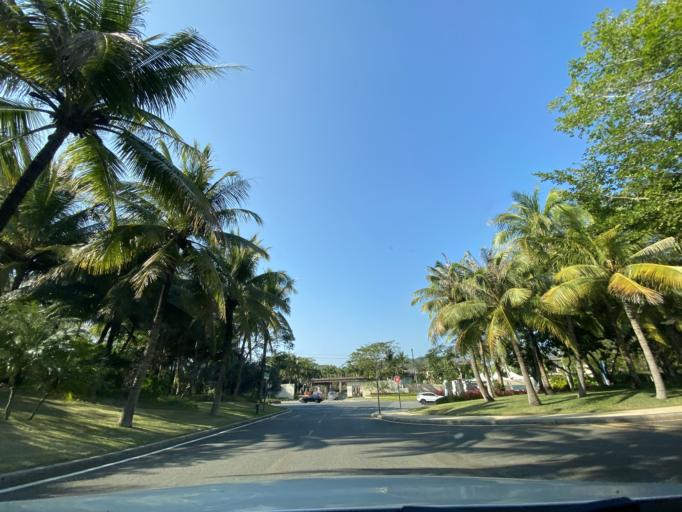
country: CN
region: Hainan
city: Yingzhou
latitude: 18.4185
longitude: 109.8962
